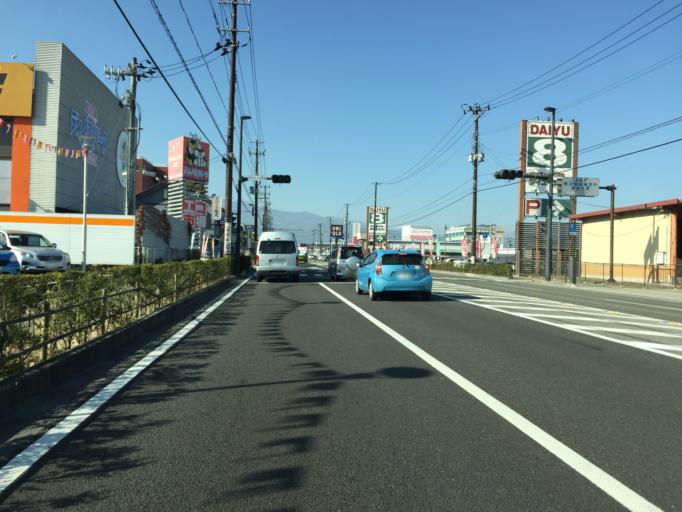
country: JP
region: Fukushima
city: Fukushima-shi
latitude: 37.7273
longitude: 140.4622
